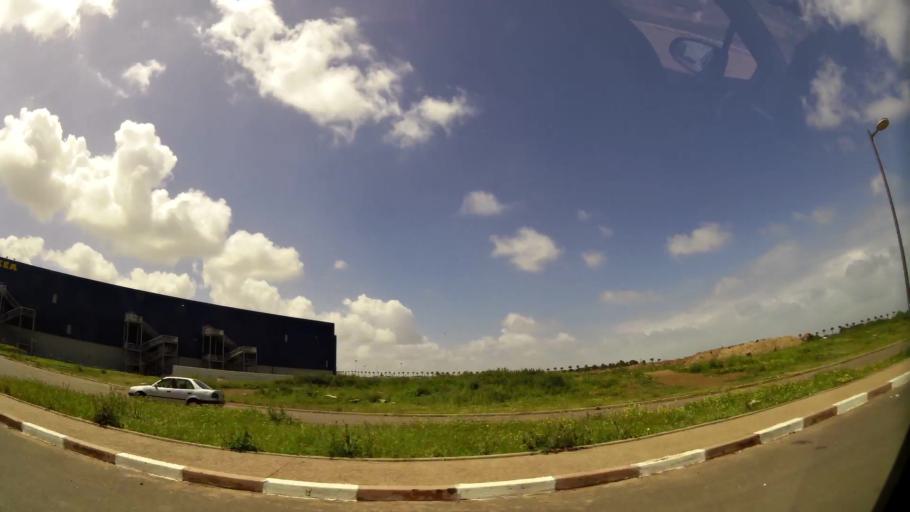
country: MA
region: Grand Casablanca
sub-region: Mediouna
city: Tit Mellil
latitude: 33.6315
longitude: -7.4588
